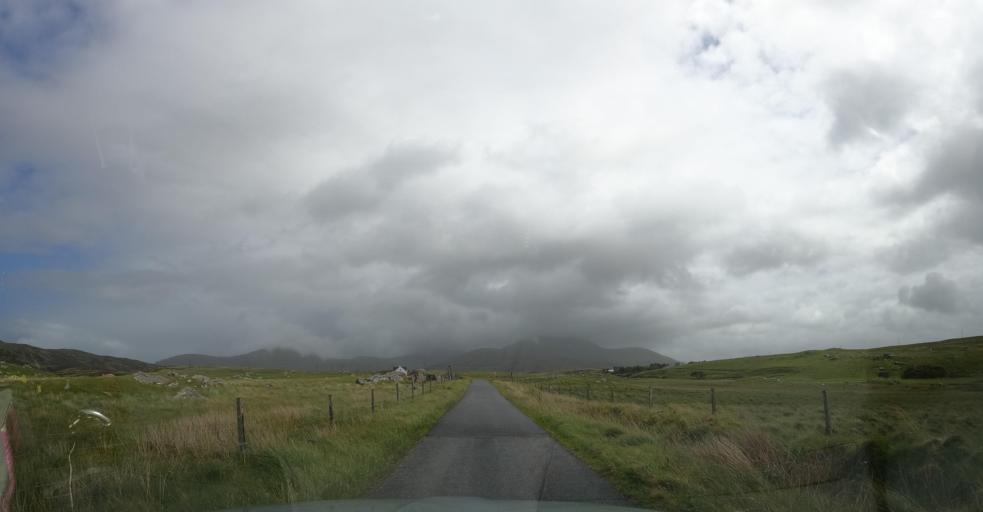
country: GB
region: Scotland
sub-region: Eilean Siar
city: Isle of South Uist
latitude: 57.2907
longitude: -7.3716
